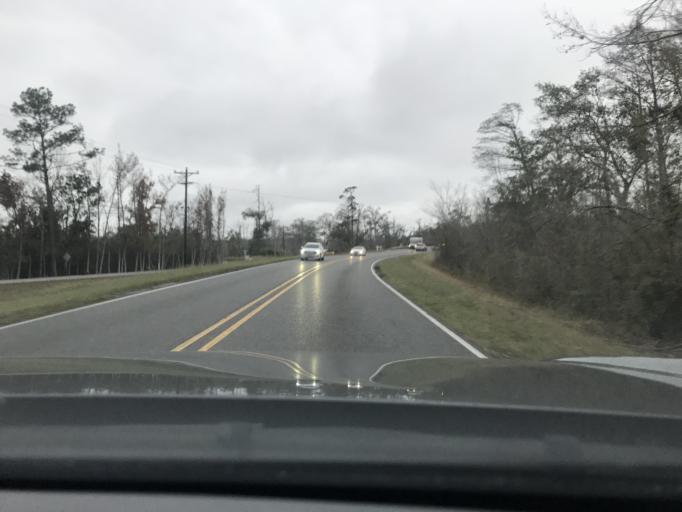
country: US
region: Louisiana
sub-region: Calcasieu Parish
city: Westlake
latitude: 30.2946
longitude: -93.2497
